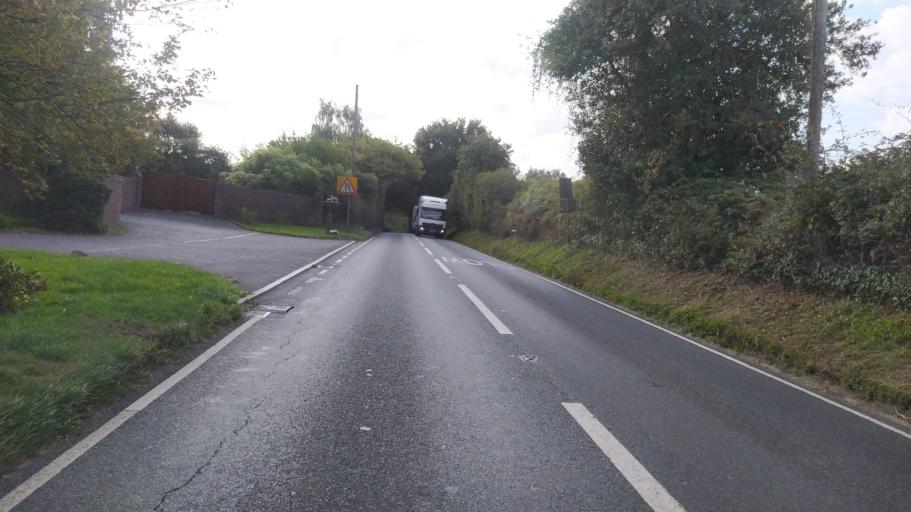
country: GB
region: England
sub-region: Dorset
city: Lytchett Matravers
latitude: 50.7603
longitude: -2.0550
